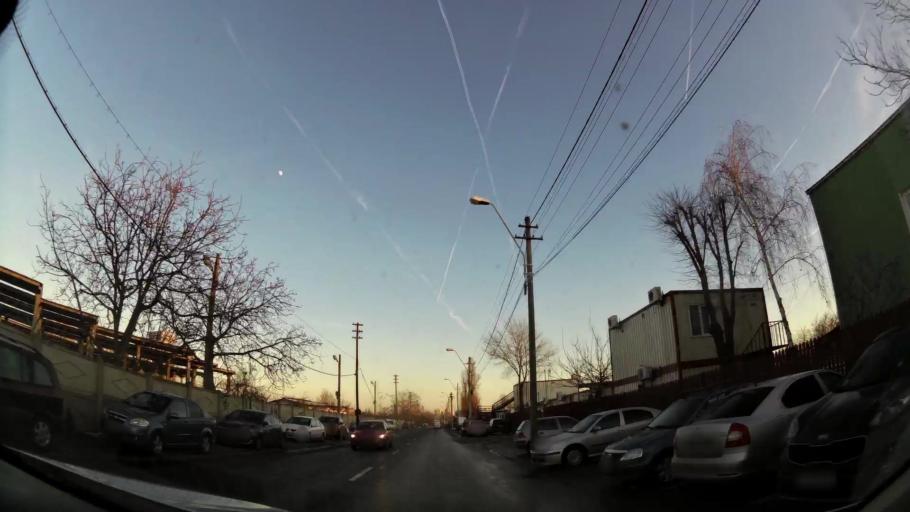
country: RO
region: Ilfov
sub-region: Comuna Fundeni-Dobroesti
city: Fundeni
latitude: 44.4507
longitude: 26.1393
